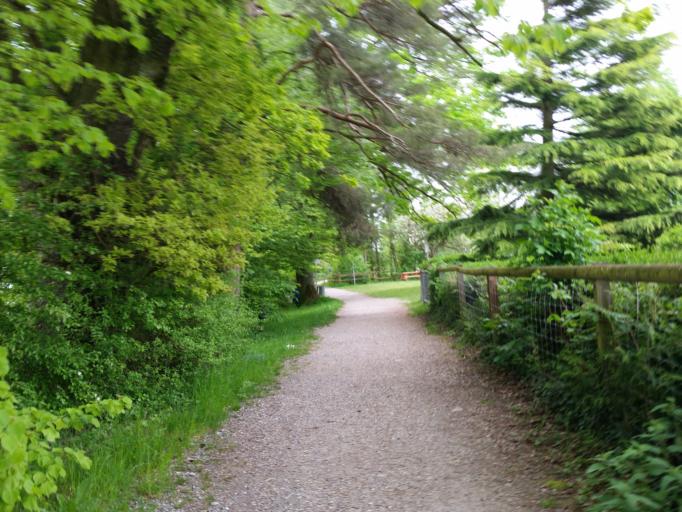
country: CH
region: Thurgau
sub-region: Kreuzlingen District
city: Guttingen
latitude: 47.6001
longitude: 9.3151
